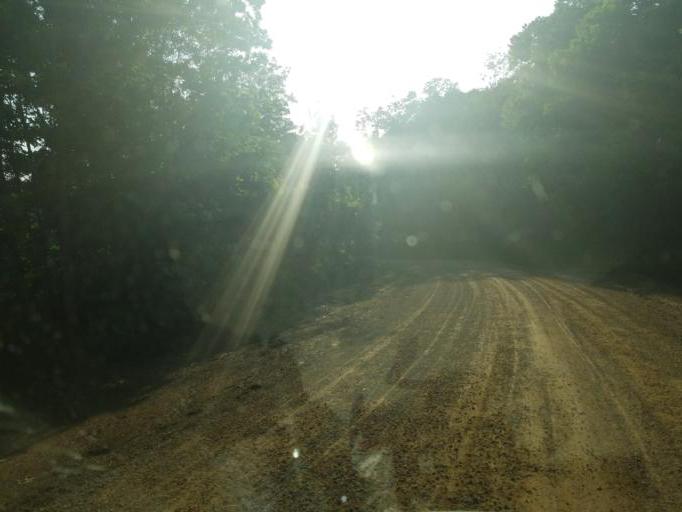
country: US
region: Wisconsin
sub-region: Vernon County
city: Hillsboro
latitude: 43.6238
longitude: -90.3308
